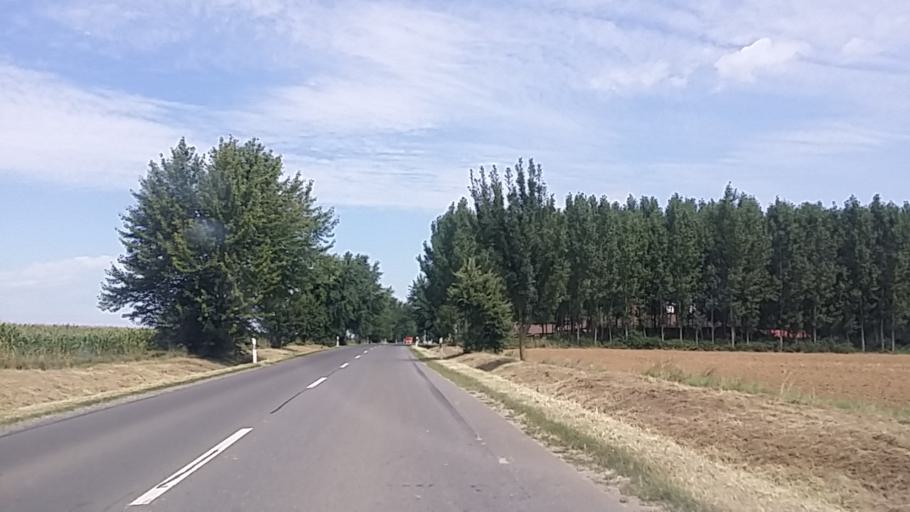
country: HU
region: Tolna
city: Dombovar
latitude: 46.3143
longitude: 18.1320
